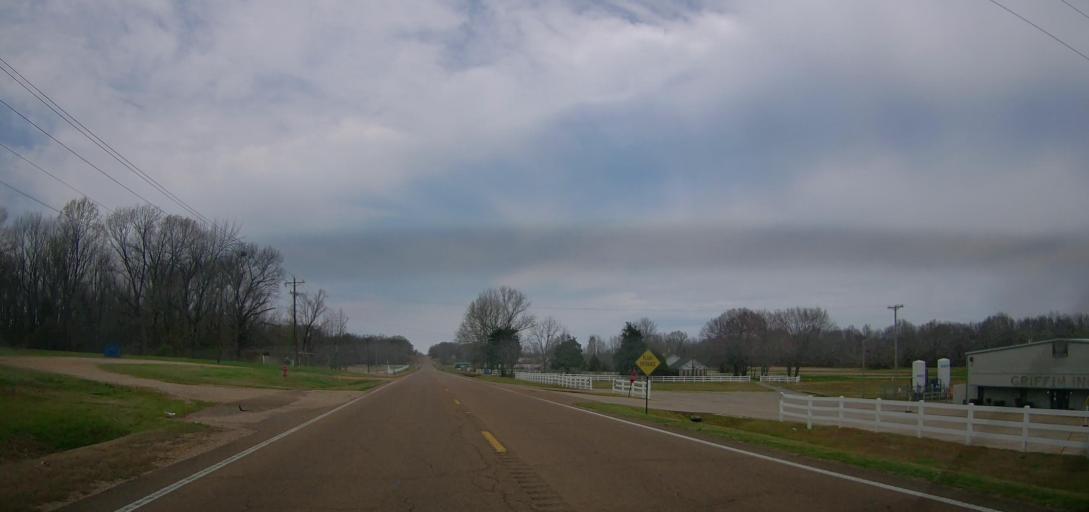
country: US
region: Mississippi
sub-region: Marshall County
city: Byhalia
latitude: 34.8549
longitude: -89.6414
